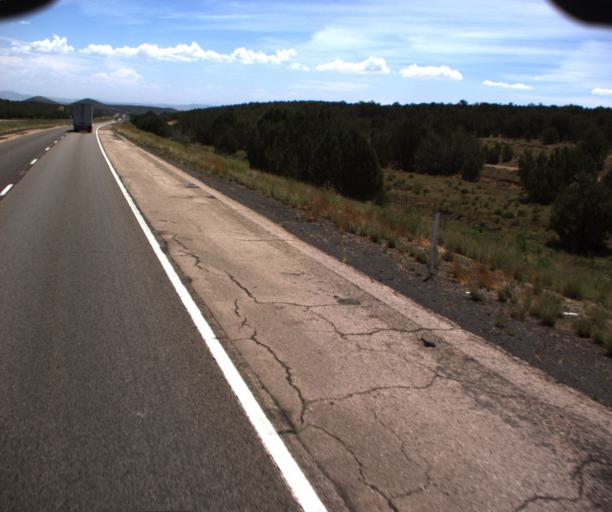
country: US
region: Arizona
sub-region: Mohave County
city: Peach Springs
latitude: 35.2916
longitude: -113.0757
